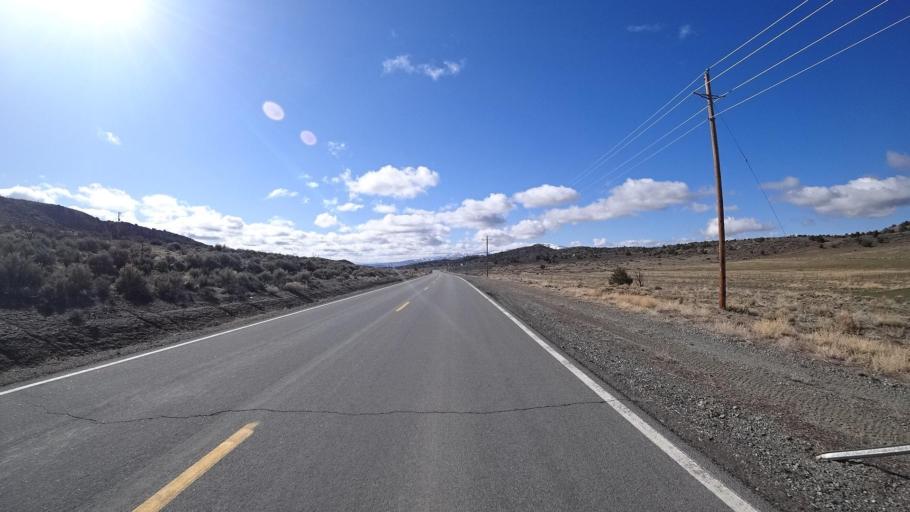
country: US
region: Nevada
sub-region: Washoe County
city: Cold Springs
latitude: 39.7504
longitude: -119.8860
